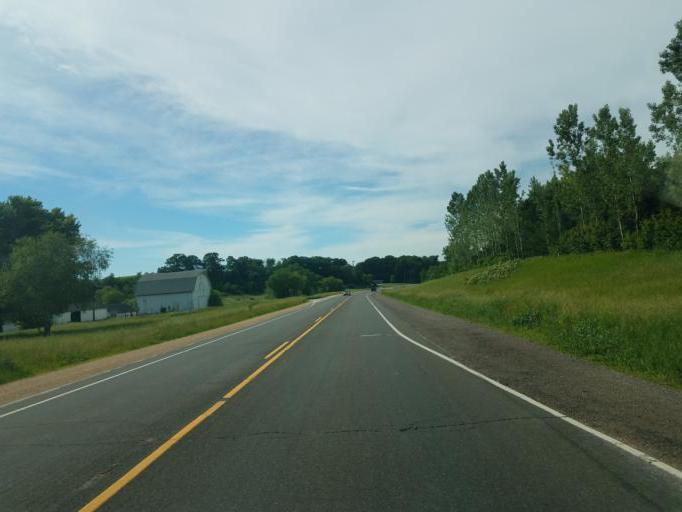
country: US
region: Wisconsin
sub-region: Monroe County
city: Tomah
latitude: 43.9258
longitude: -90.5009
